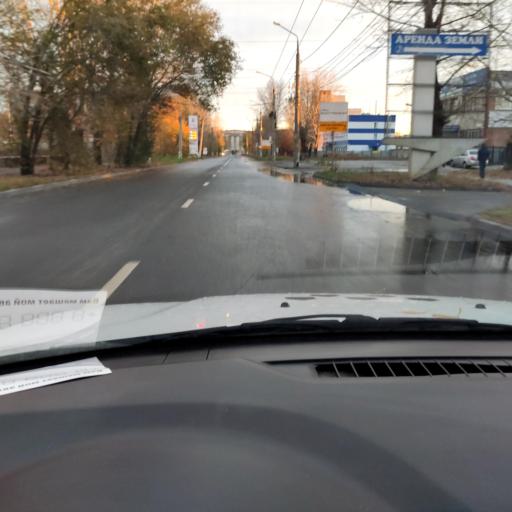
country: RU
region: Samara
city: Tol'yatti
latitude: 53.5155
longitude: 49.4558
